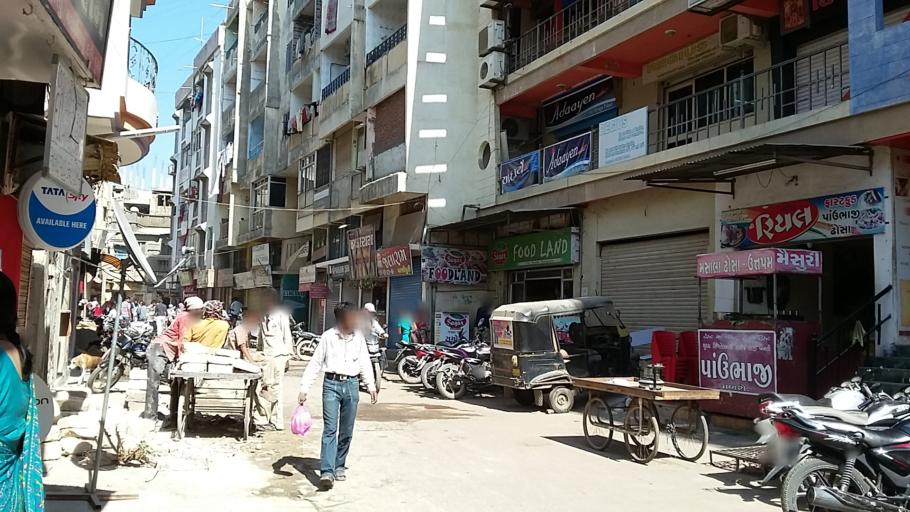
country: IN
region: Gujarat
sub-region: Junagadh
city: Junagadh
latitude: 21.5166
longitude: 70.4617
